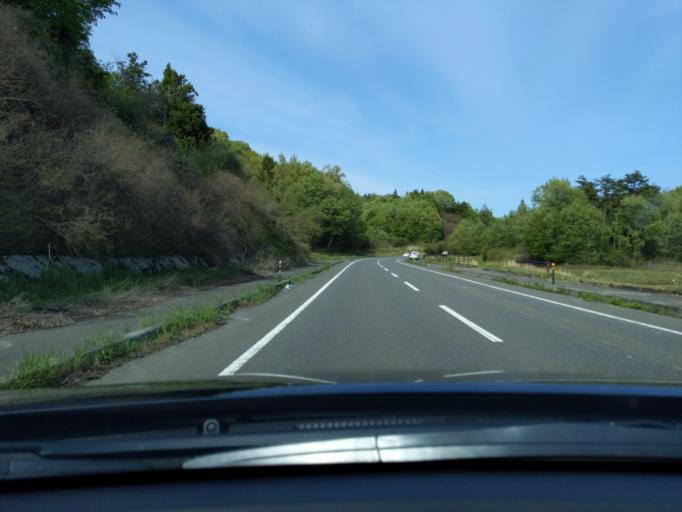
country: JP
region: Fukushima
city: Koriyama
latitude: 37.3550
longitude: 140.4256
